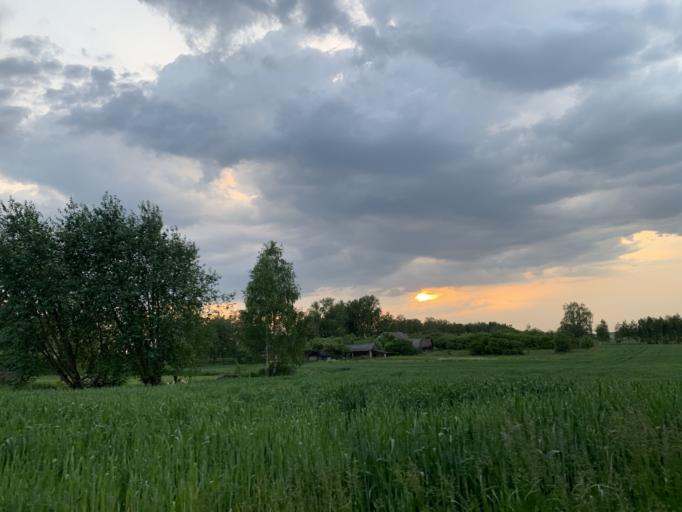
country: BY
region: Minsk
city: Tsimkavichy
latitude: 53.1272
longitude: 26.8831
